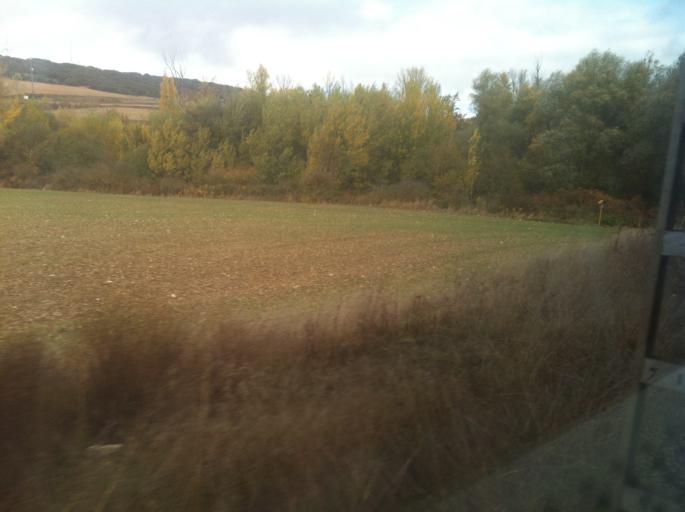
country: ES
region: Castille and Leon
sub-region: Provincia de Burgos
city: Santa Olalla de Bureba
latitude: 42.4621
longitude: -3.4484
